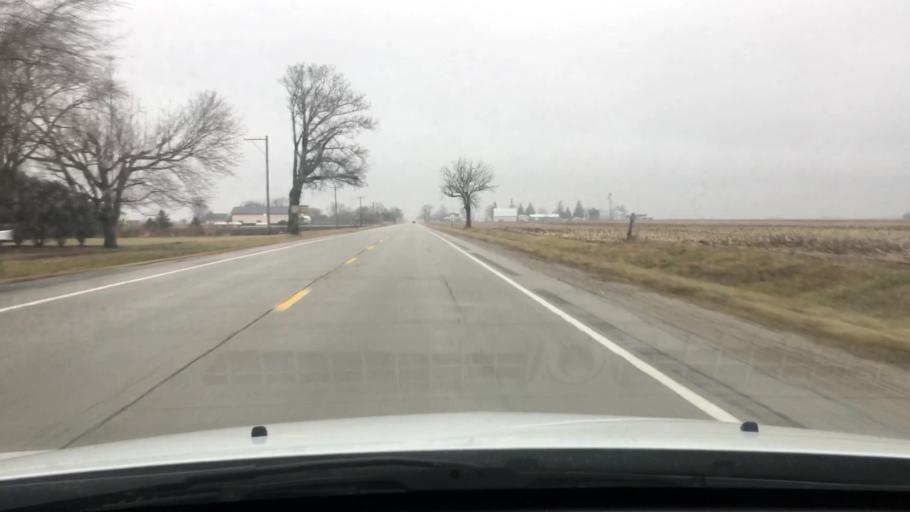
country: US
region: Illinois
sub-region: Livingston County
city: Flanagan
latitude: 40.8707
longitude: -88.8738
